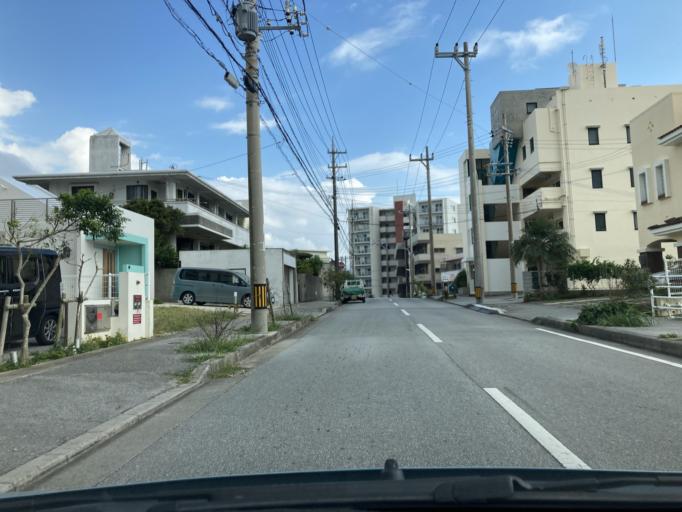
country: JP
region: Okinawa
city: Ginowan
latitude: 26.2409
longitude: 127.7616
